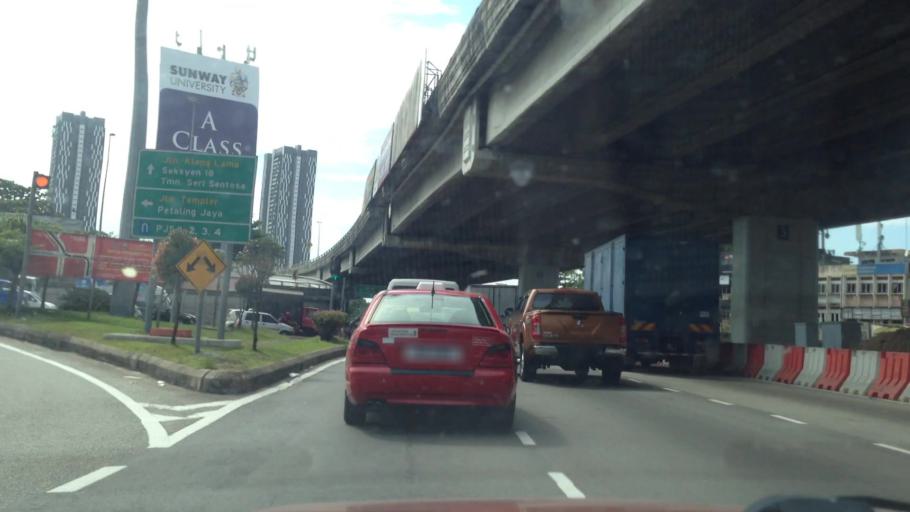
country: MY
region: Selangor
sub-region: Petaling
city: Petaling Jaya
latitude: 3.0818
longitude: 101.6552
